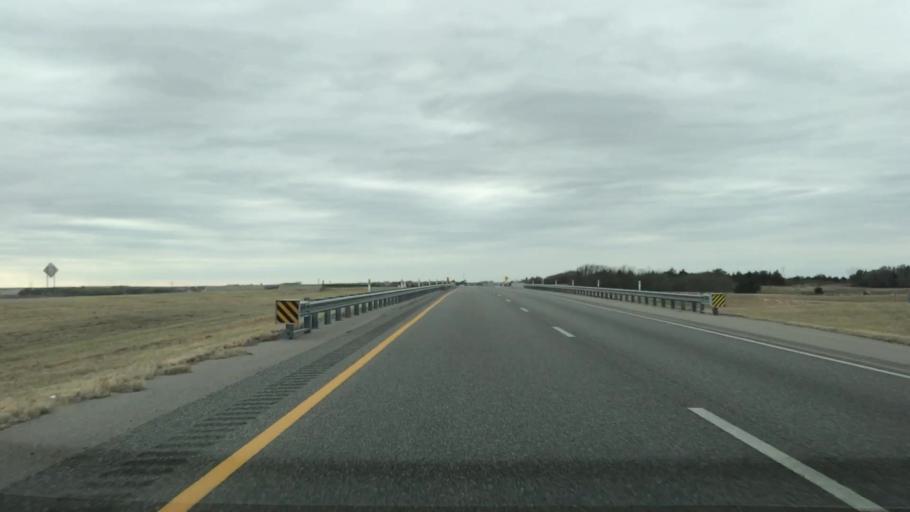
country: US
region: Oklahoma
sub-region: Beckham County
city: Erick
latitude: 35.2266
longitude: -99.9109
